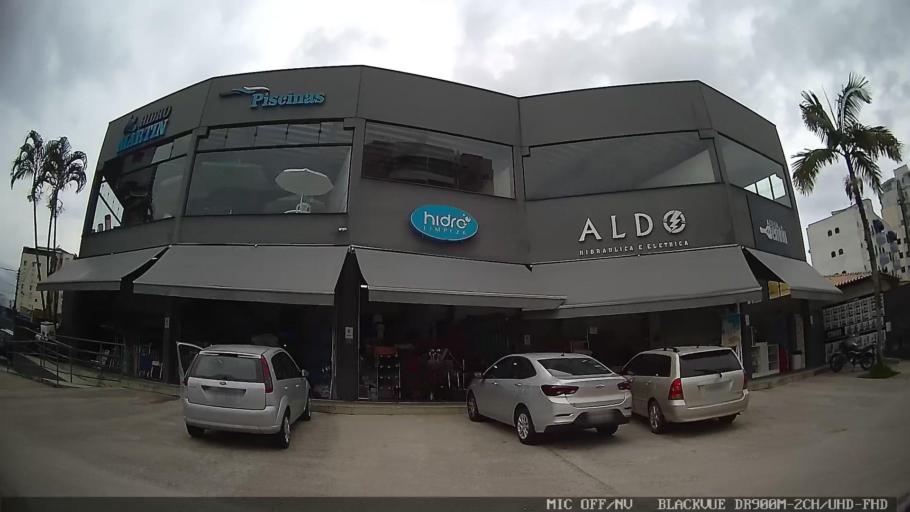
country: BR
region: Sao Paulo
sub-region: Caraguatatuba
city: Caraguatatuba
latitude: -23.6300
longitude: -45.3872
